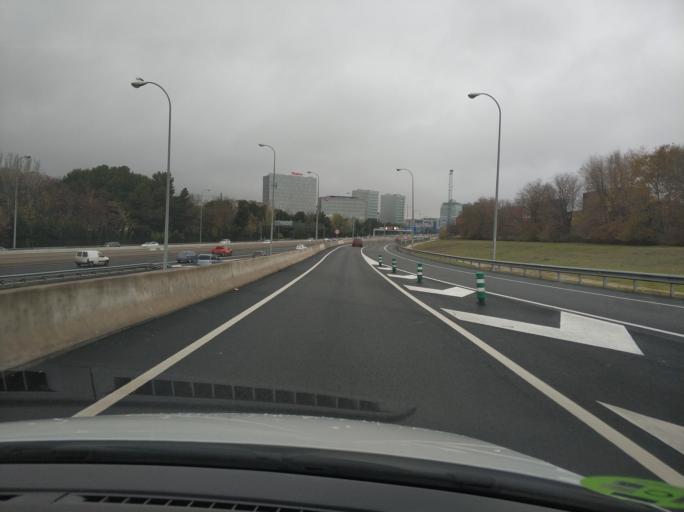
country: ES
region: Madrid
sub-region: Provincia de Madrid
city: Usera
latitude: 40.3858
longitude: -3.6813
